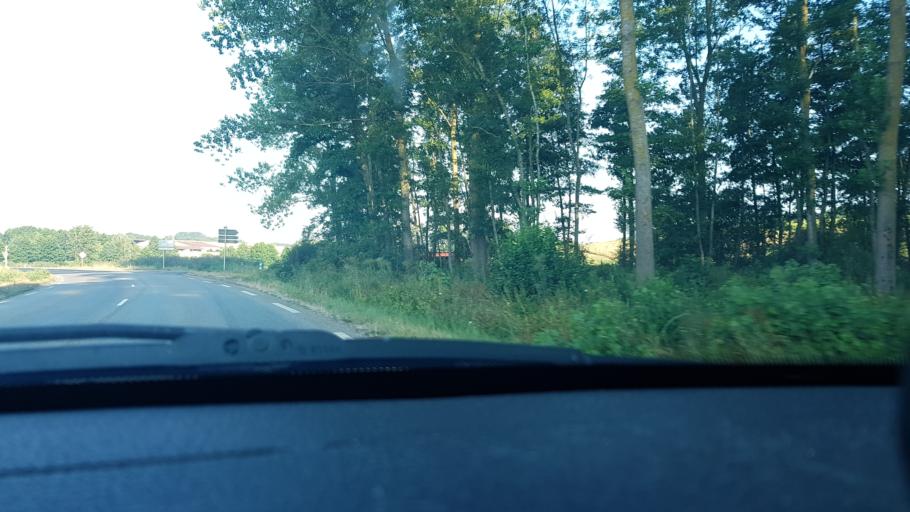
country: FR
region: Lorraine
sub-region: Departement des Vosges
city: Charmes
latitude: 48.3615
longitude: 6.2279
